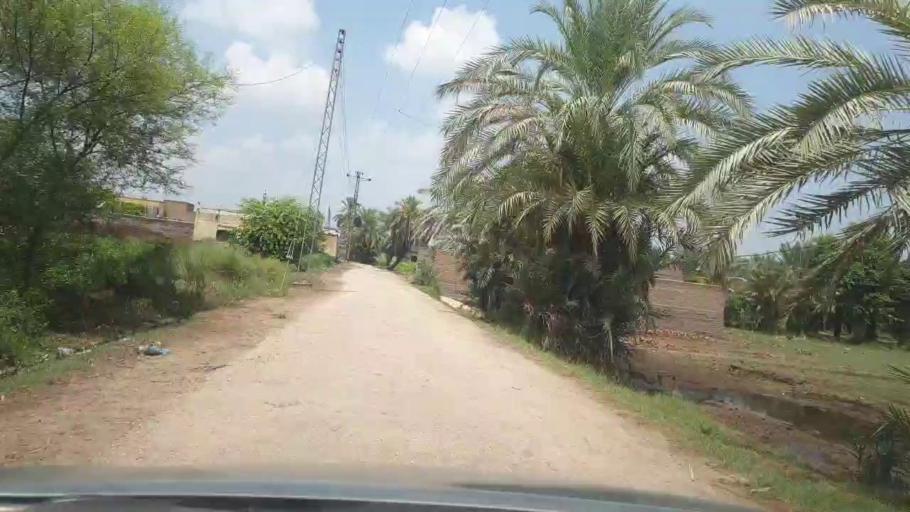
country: PK
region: Sindh
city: Pir jo Goth
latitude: 27.6073
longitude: 68.6133
